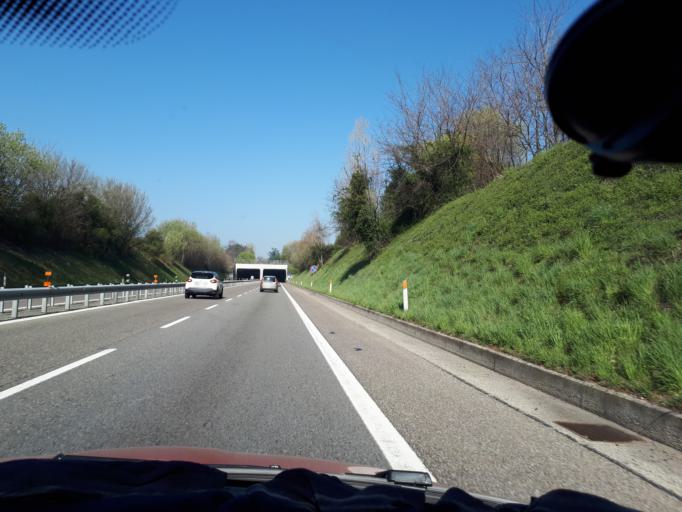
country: IT
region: Lombardy
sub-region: Provincia di Monza e Brianza
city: Lentate sul Seveso
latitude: 45.6719
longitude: 9.1147
